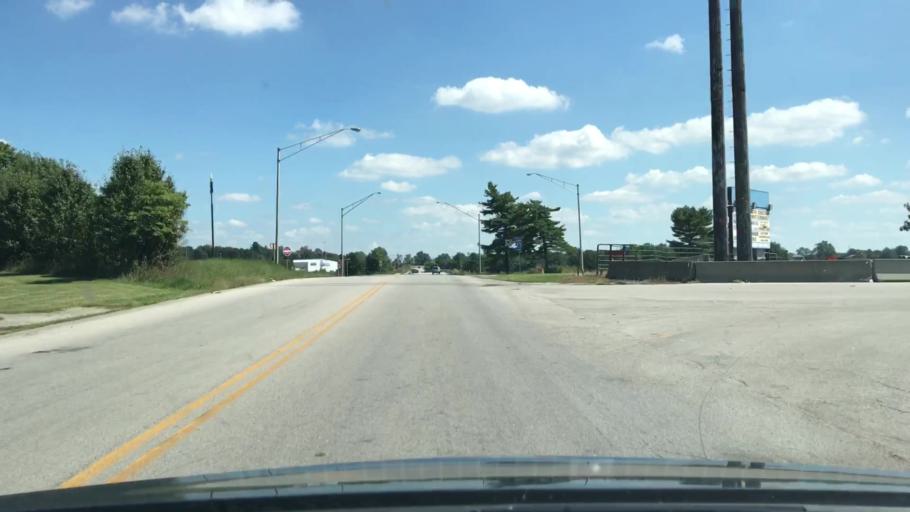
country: US
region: Kentucky
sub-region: Hardin County
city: Elizabethtown
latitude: 37.5971
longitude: -85.8719
